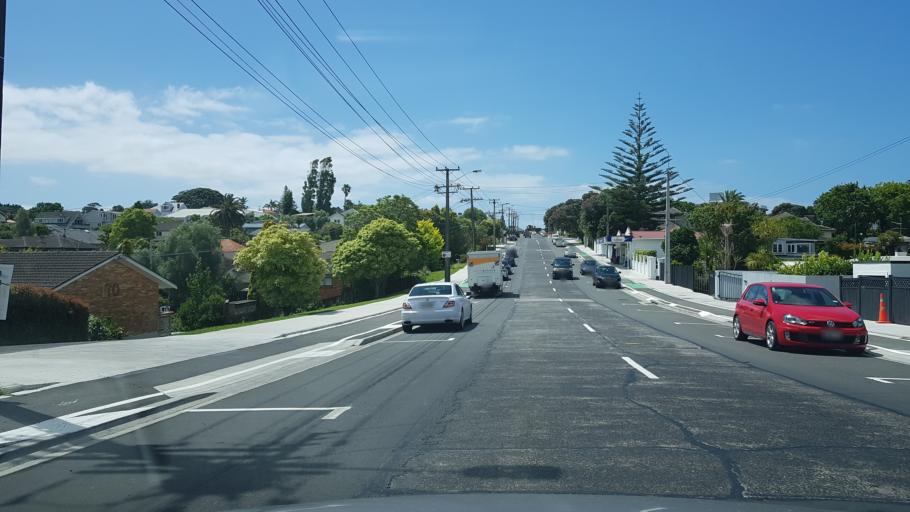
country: NZ
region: Auckland
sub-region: Auckland
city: North Shore
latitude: -36.8147
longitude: 174.7453
